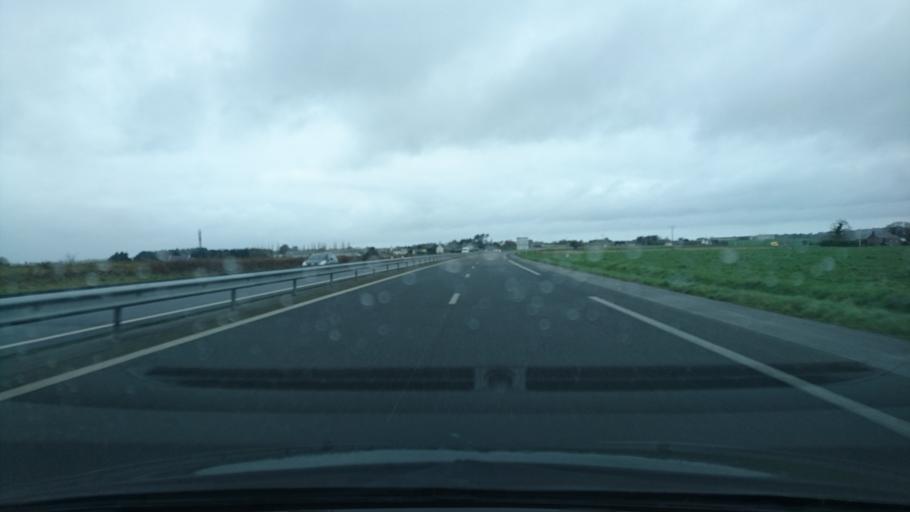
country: FR
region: Brittany
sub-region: Departement du Finistere
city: Taule
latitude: 48.6105
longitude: -3.8906
